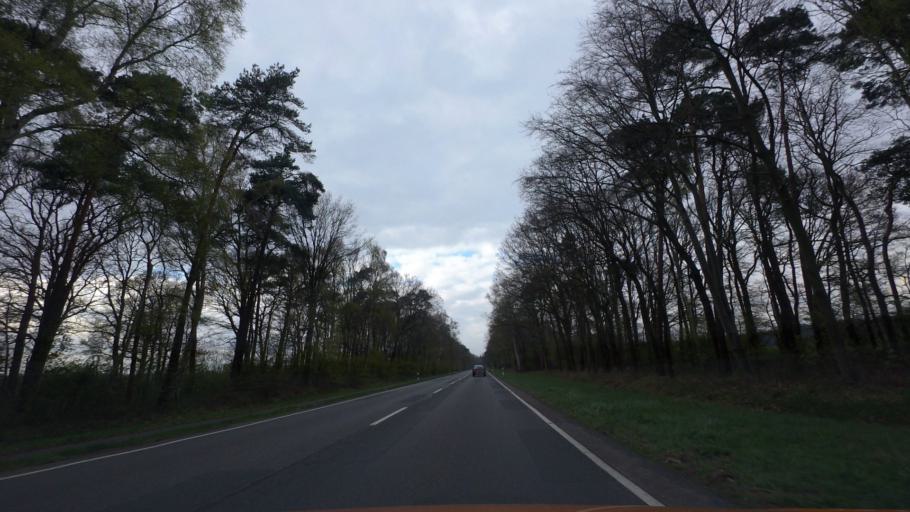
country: DE
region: Lower Saxony
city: Molbergen
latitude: 52.9296
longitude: 7.9490
